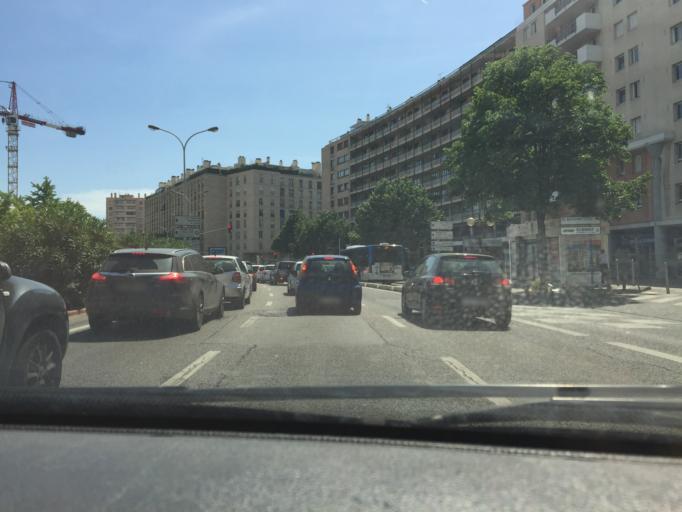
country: FR
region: Provence-Alpes-Cote d'Azur
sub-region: Departement des Bouches-du-Rhone
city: Marseille 05
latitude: 43.2914
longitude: 5.4001
